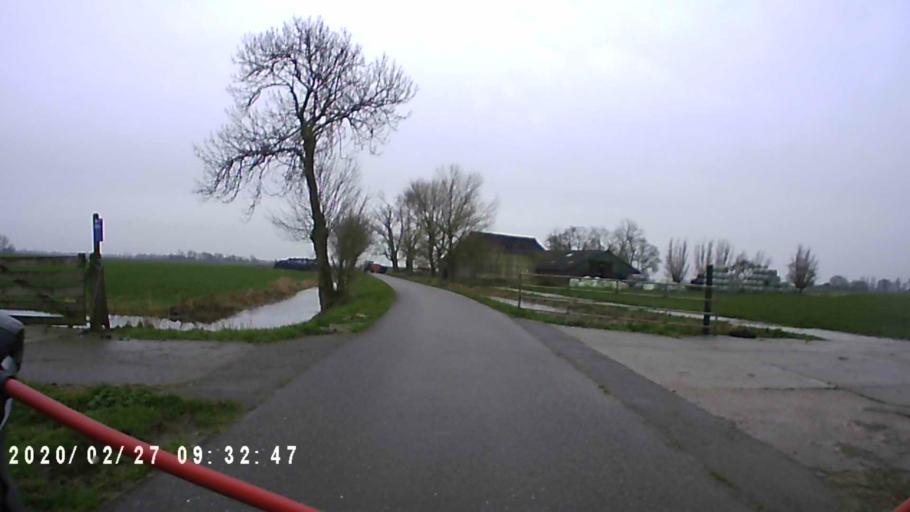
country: NL
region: Groningen
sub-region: Gemeente Zuidhorn
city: Aduard
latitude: 53.2898
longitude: 6.4489
